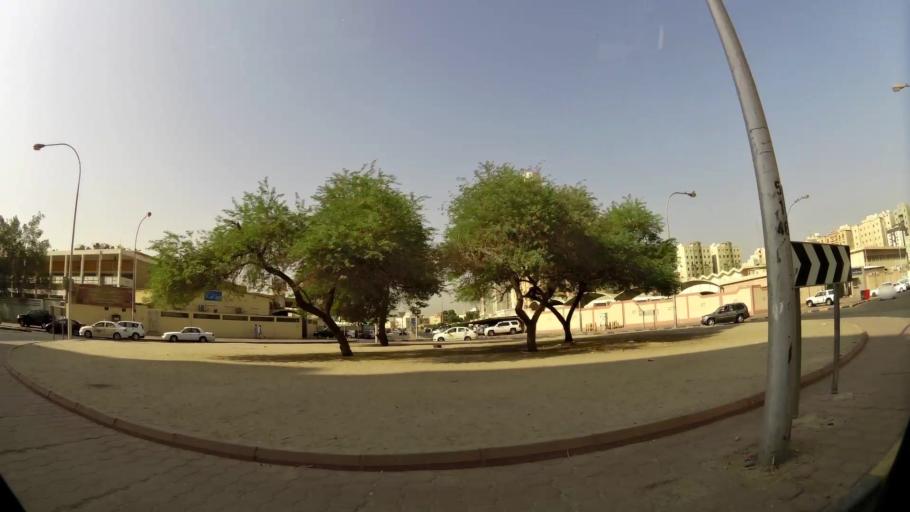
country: KW
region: Muhafazat Hawalli
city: Hawalli
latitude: 29.3255
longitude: 48.0142
